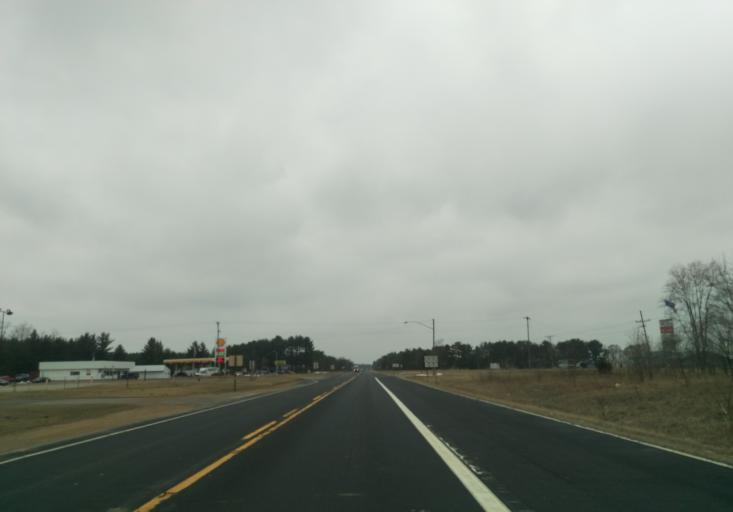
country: US
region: Wisconsin
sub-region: Sauk County
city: Spring Green
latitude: 43.1913
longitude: -90.1975
